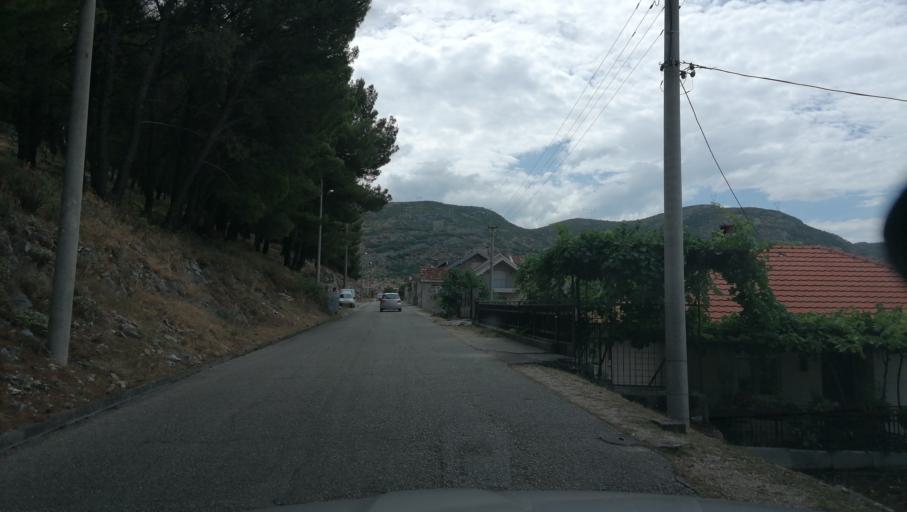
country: BA
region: Republika Srpska
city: Trebinje
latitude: 42.7106
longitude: 18.3574
